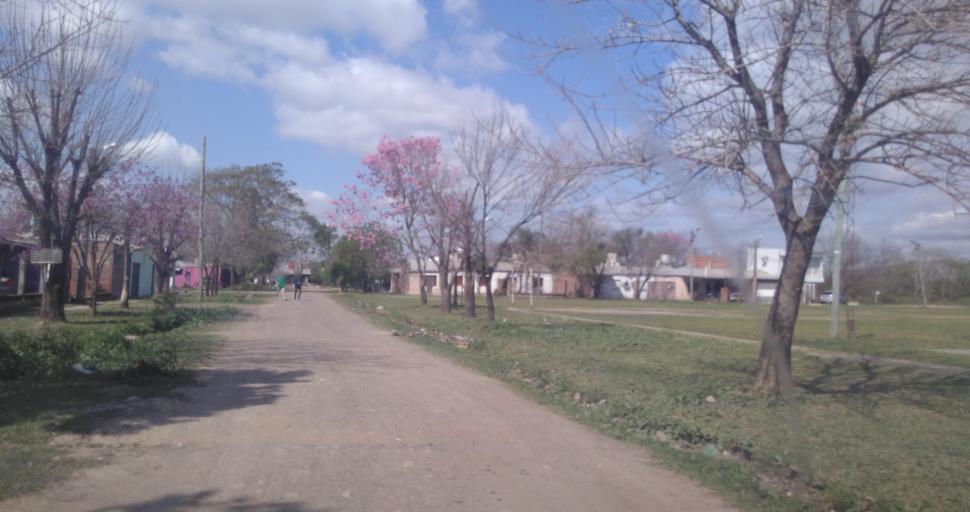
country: AR
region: Chaco
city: Fontana
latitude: -27.4304
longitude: -59.0349
